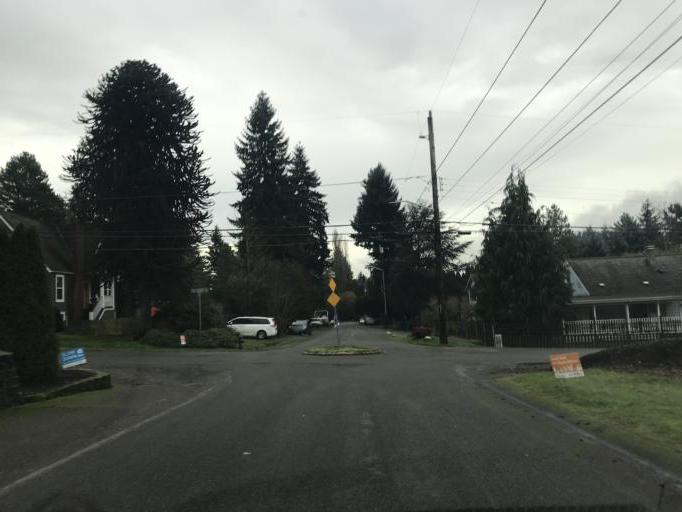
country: US
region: Washington
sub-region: King County
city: Lake Forest Park
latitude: 47.7157
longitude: -122.2873
